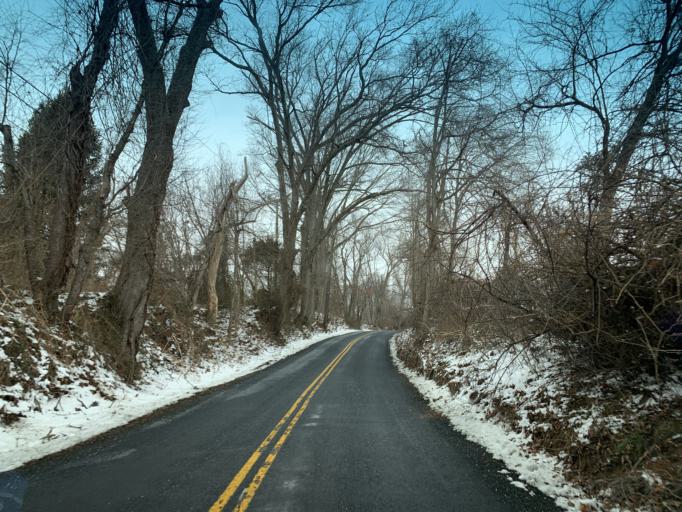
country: US
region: Pennsylvania
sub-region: York County
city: Susquehanna Trails
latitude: 39.7121
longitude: -76.2997
